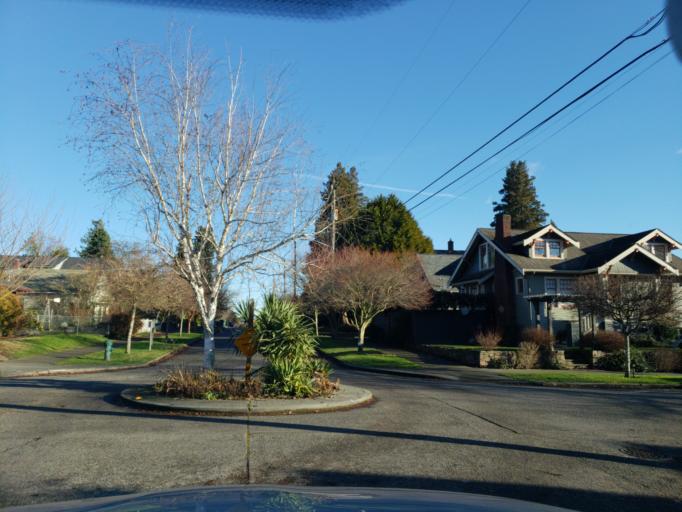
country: US
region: Washington
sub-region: King County
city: Shoreline
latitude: 47.6803
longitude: -122.3500
